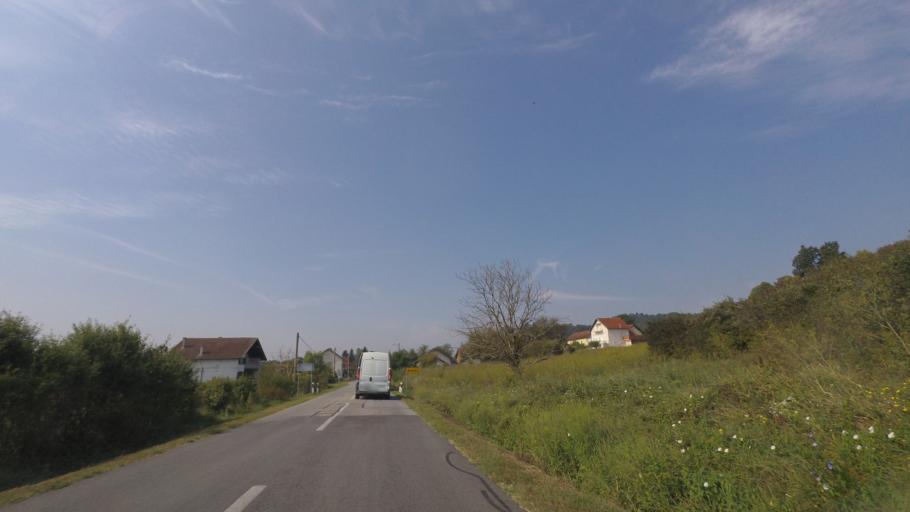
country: BA
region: Republika Srpska
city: Dobrljin
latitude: 45.1443
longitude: 16.4481
